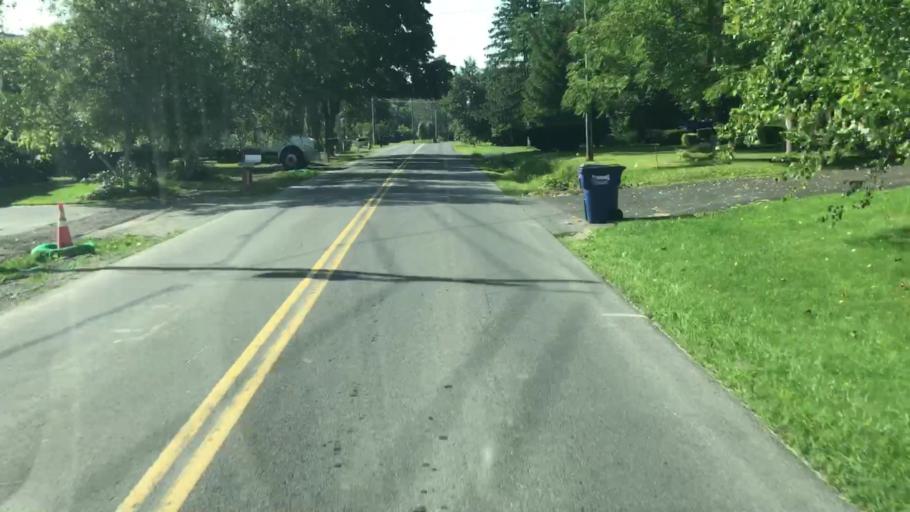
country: US
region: New York
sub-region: Cayuga County
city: Melrose Park
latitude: 42.9095
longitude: -76.5292
